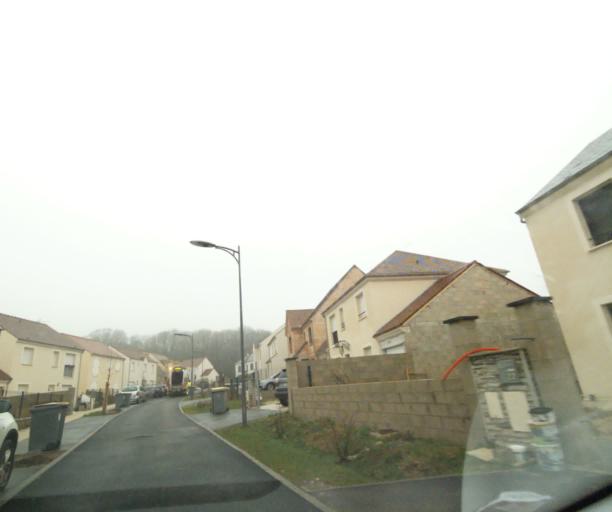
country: FR
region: Ile-de-France
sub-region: Departement de Seine-et-Marne
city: Othis
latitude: 49.0645
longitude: 2.6707
